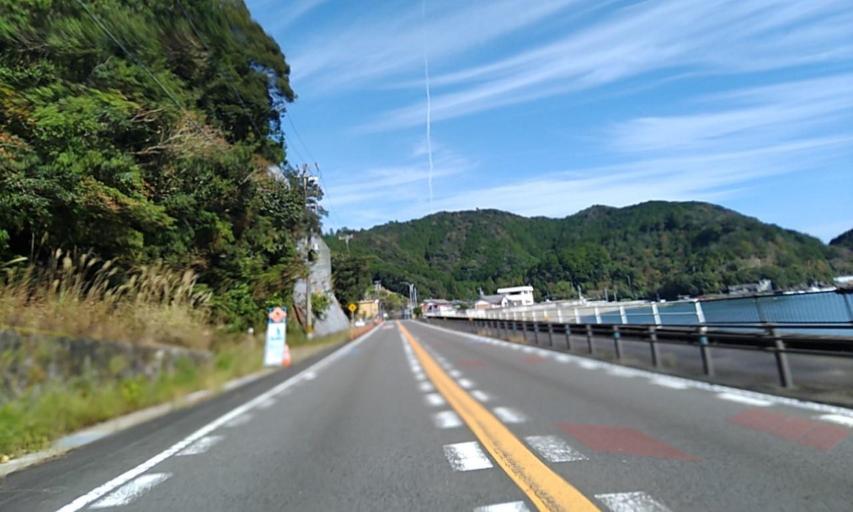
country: JP
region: Mie
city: Owase
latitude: 34.1621
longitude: 136.2783
